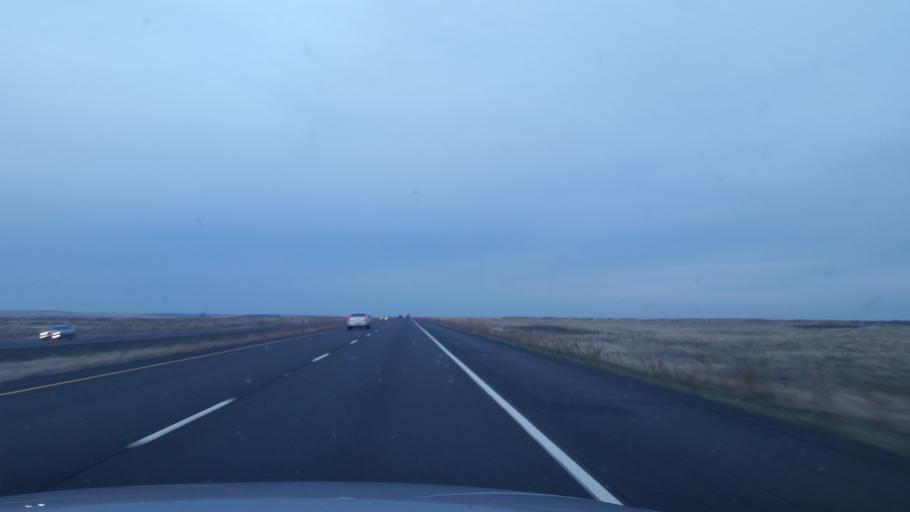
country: US
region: Washington
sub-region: Adams County
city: Ritzville
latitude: 47.2245
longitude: -118.1816
